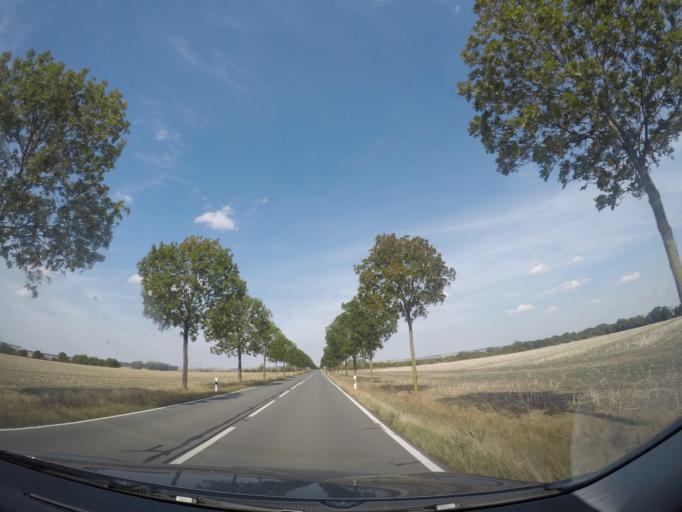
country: DE
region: Saxony-Anhalt
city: Langeln
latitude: 51.9217
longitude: 10.7984
